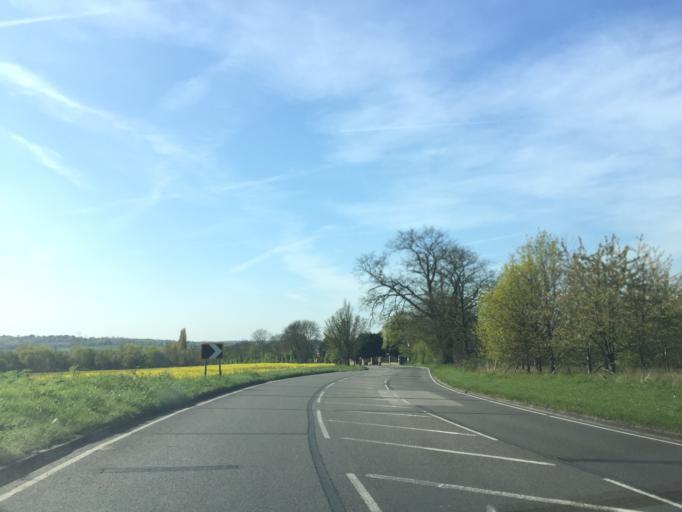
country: GB
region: England
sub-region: Essex
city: Theydon Bois
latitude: 51.6632
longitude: 0.1146
